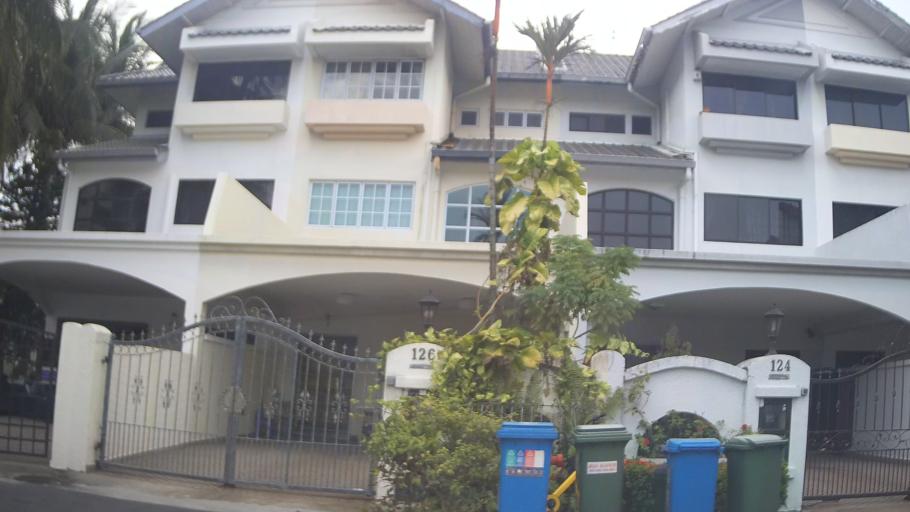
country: MY
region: Johor
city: Kampung Pasir Gudang Baru
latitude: 1.3857
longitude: 103.8574
